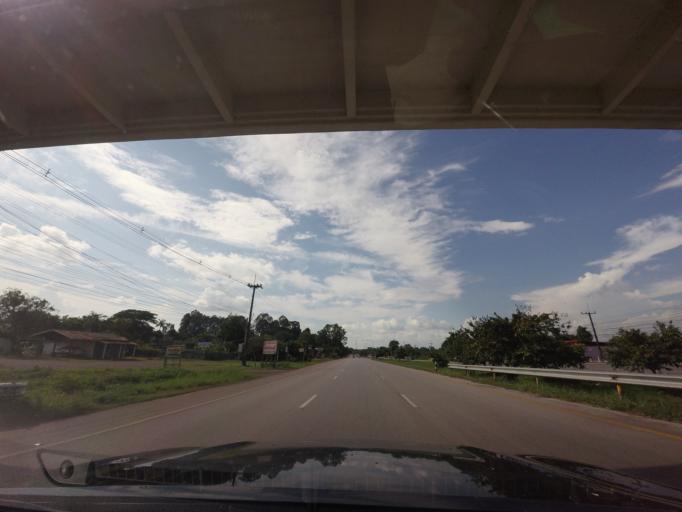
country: TH
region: Nong Khai
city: Sa Khrai
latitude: 17.6759
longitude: 102.7885
